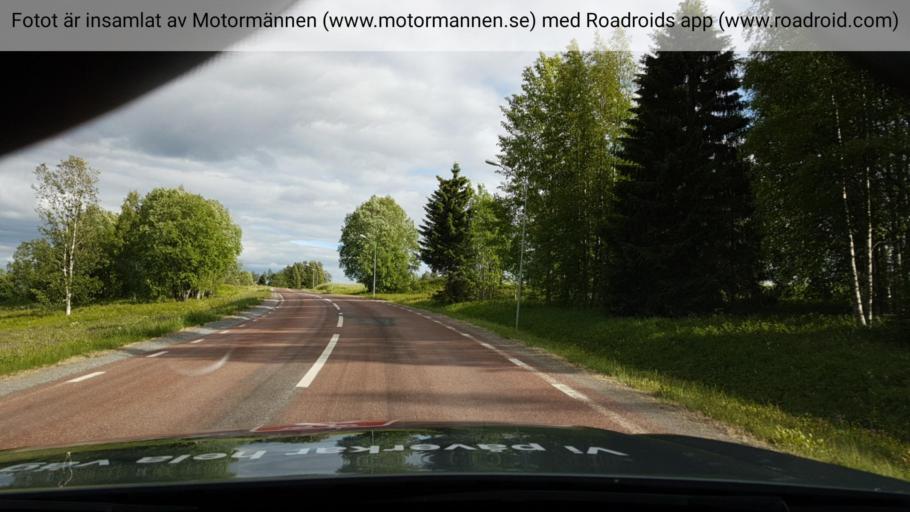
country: SE
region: Jaemtland
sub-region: Stroemsunds Kommun
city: Stroemsund
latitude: 63.7362
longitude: 15.4856
